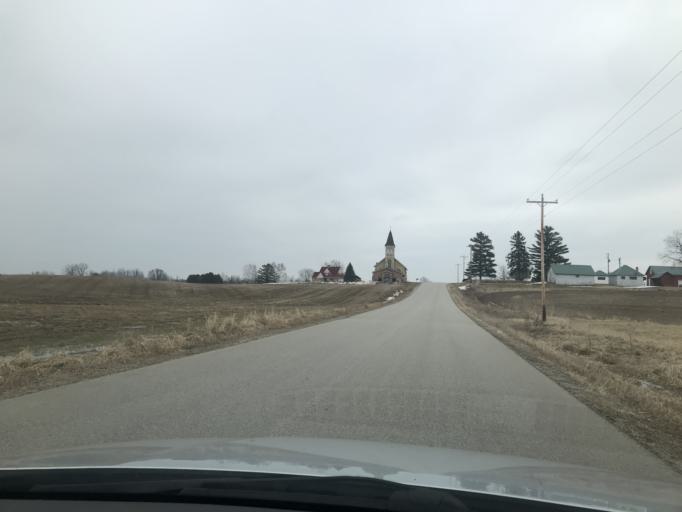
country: US
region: Wisconsin
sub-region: Marinette County
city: Peshtigo
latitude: 45.0272
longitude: -87.8736
